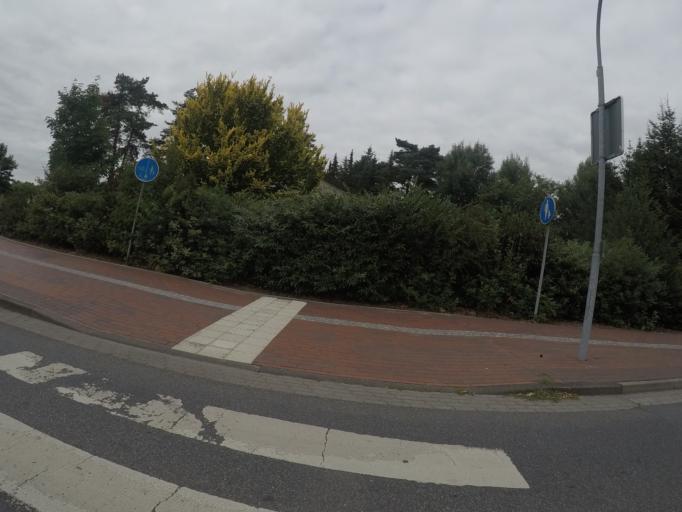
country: DE
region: Lower Saxony
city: Hemmoor
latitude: 53.6858
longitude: 9.1594
